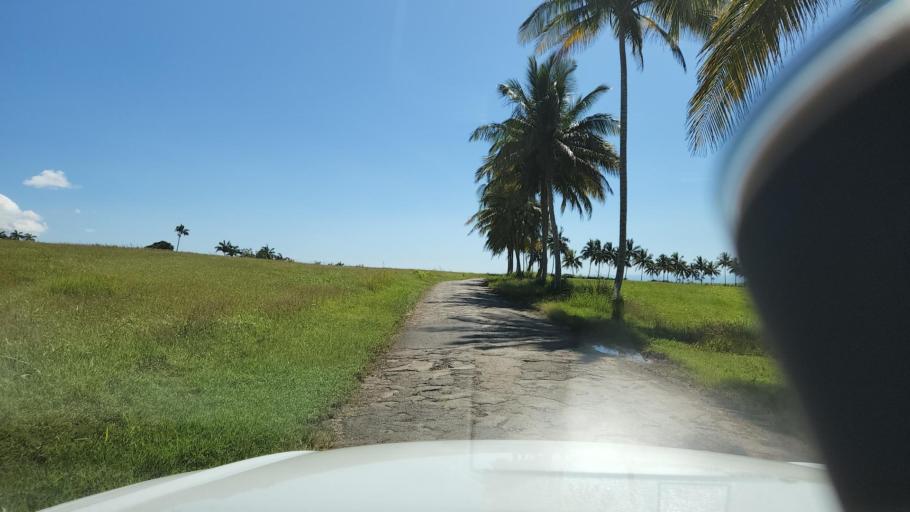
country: BB
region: Saint Thomas
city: Welchman Hall
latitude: 13.1927
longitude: -59.5895
